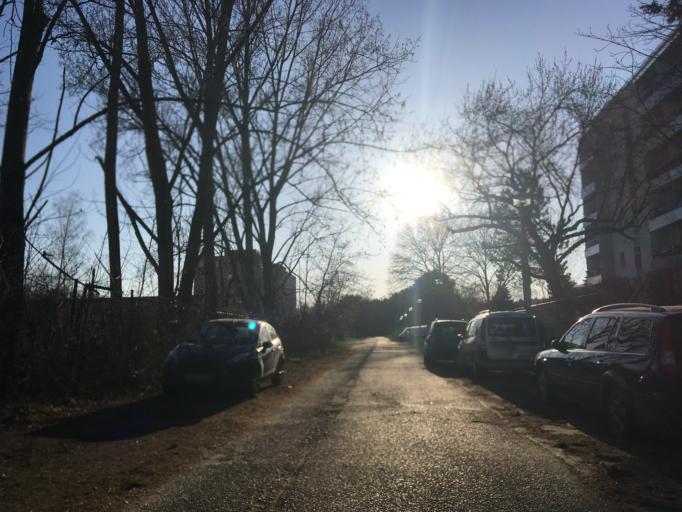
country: DE
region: Berlin
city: Buch
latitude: 52.6375
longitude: 13.4825
